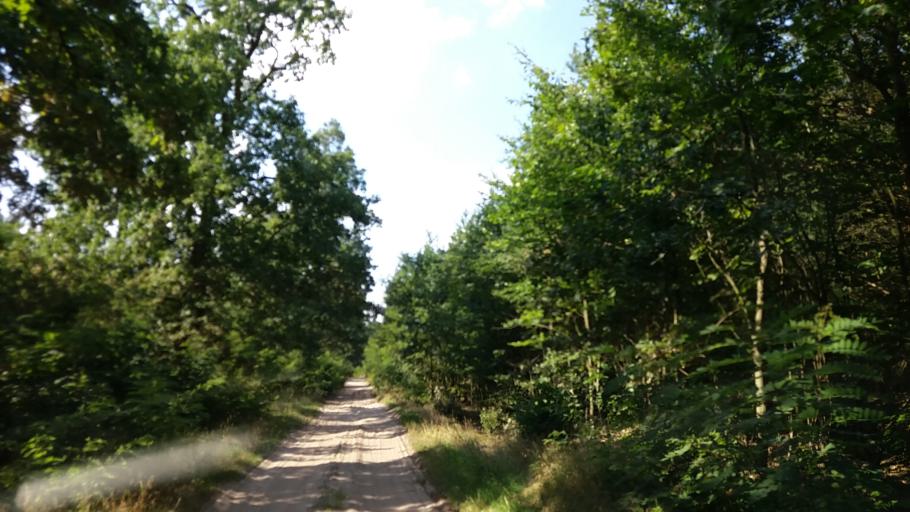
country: PL
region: West Pomeranian Voivodeship
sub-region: Powiat choszczenski
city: Krzecin
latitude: 53.0973
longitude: 15.4250
